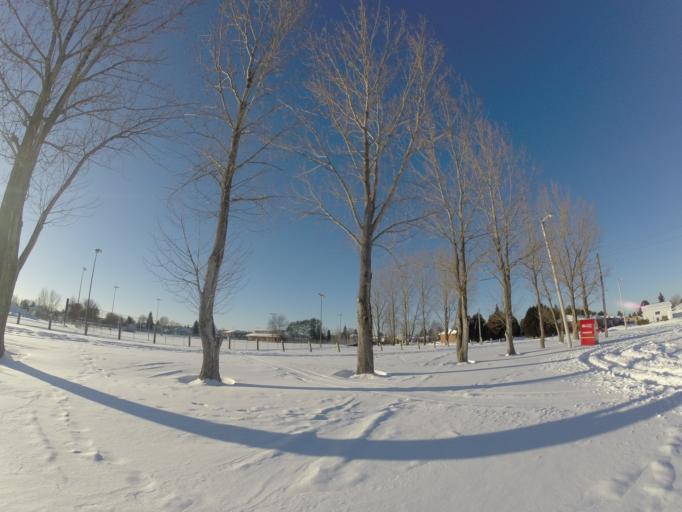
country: CA
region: Ontario
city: Rayside-Balfour
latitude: 46.5753
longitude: -81.1925
